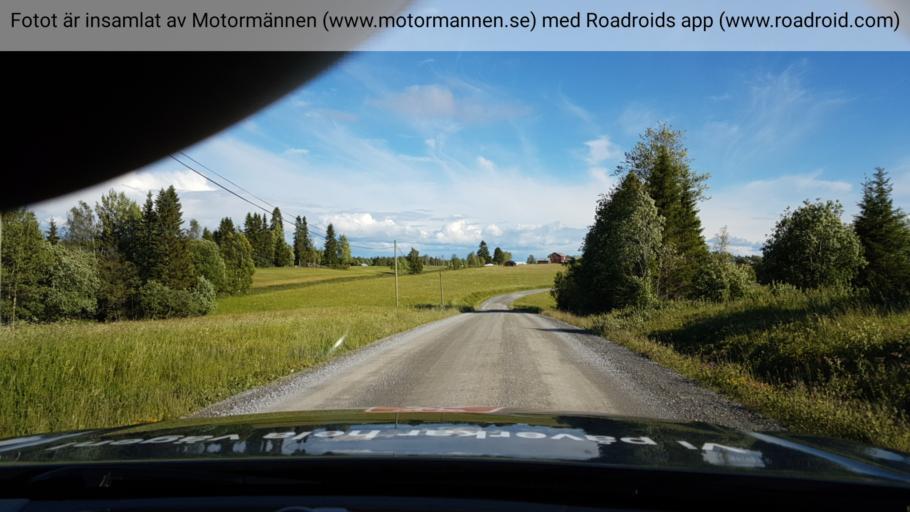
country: SE
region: Jaemtland
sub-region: Bergs Kommun
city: Hoverberg
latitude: 63.0139
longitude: 14.3854
